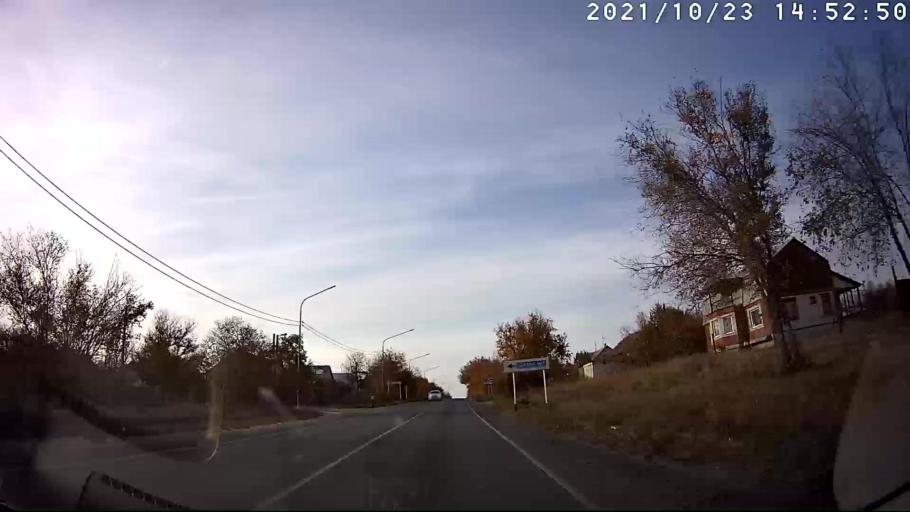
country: RU
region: Volgograd
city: Volgograd
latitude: 48.4379
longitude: 44.4365
